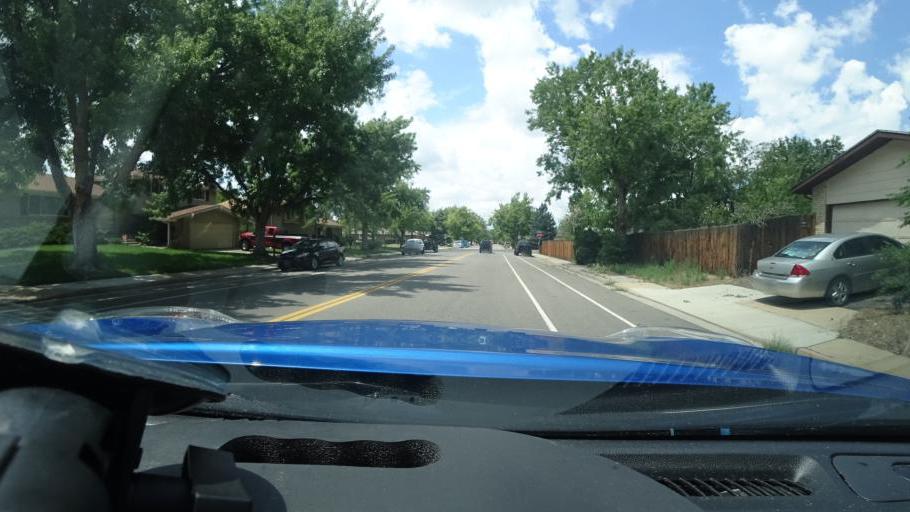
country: US
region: Colorado
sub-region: Adams County
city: Aurora
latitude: 39.7016
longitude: -104.8385
